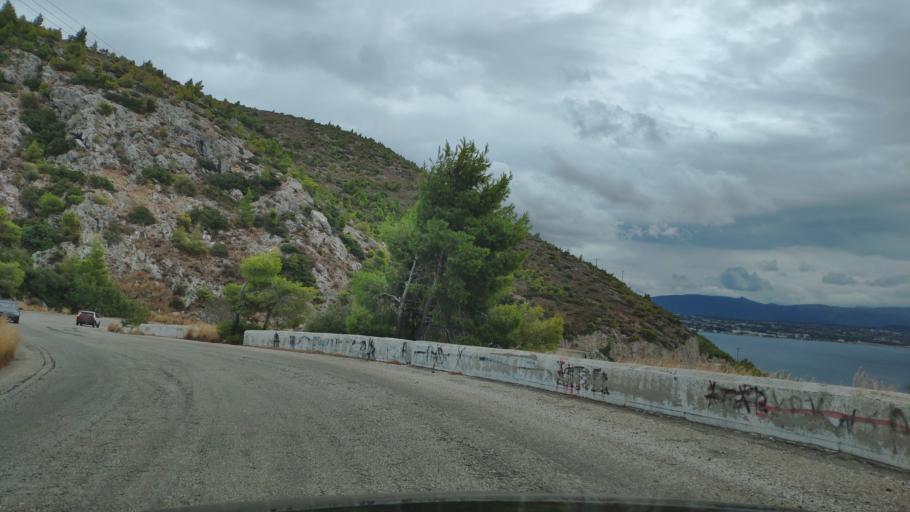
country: GR
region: Peloponnese
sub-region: Nomos Korinthias
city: Perachora
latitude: 37.9980
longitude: 22.9480
